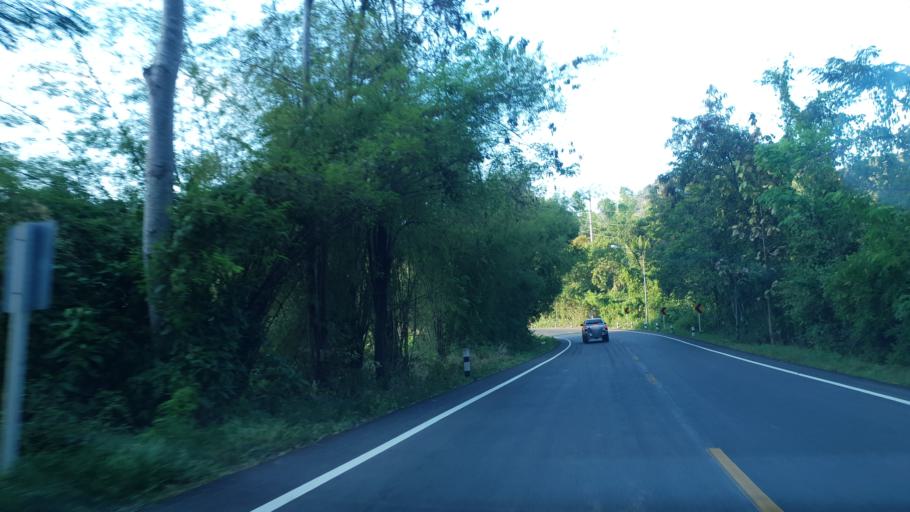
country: TH
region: Loei
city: Dan Sai
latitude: 17.2308
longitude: 101.0557
